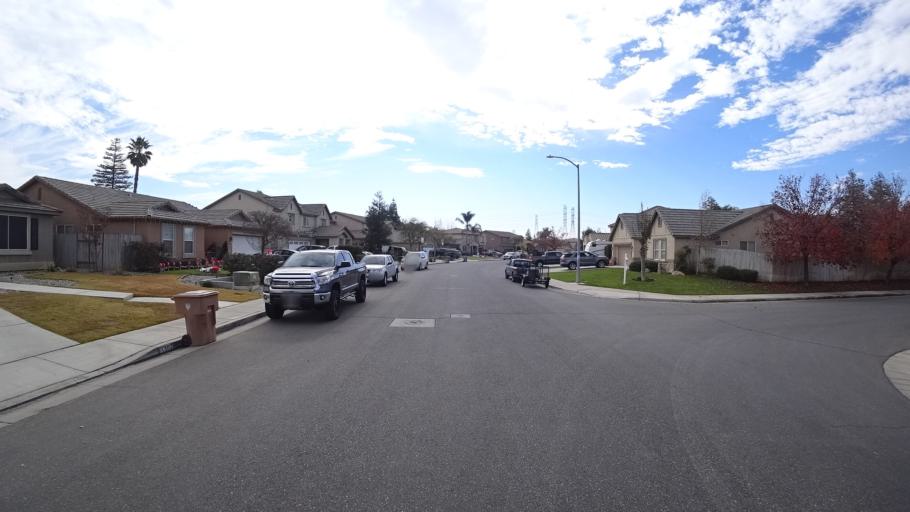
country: US
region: California
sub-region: Kern County
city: Rosedale
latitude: 35.3896
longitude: -119.1307
